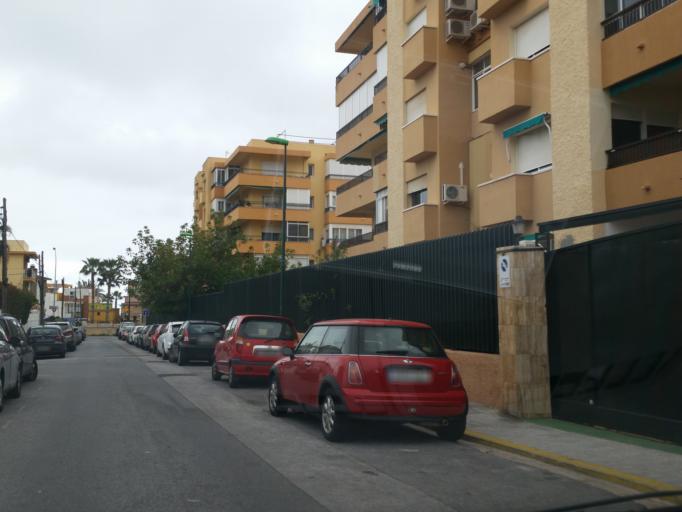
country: ES
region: Andalusia
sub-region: Provincia de Malaga
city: Malaga
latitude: 36.7211
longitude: -4.3678
